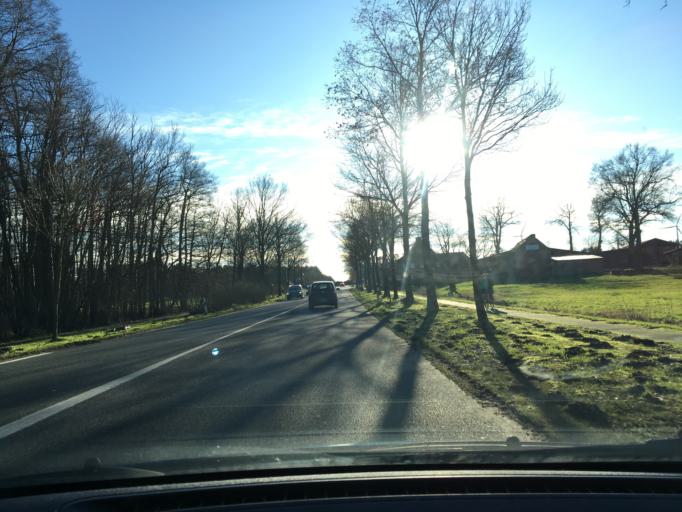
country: DE
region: Lower Saxony
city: Melbeck
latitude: 53.2107
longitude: 10.4053
